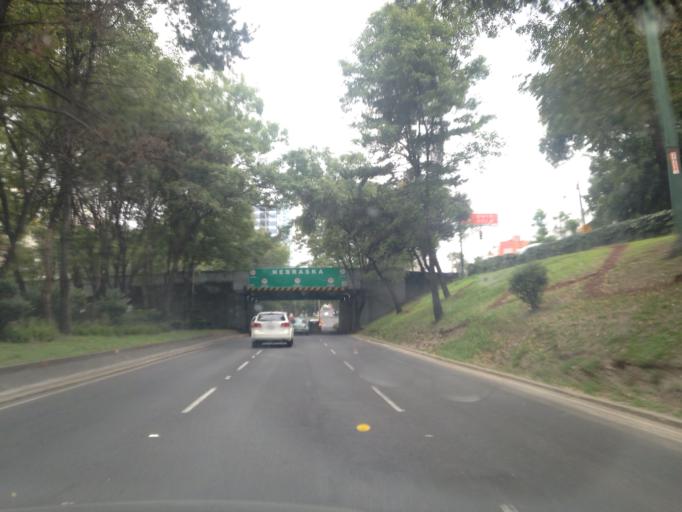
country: MX
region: Mexico City
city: Colonia del Valle
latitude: 19.3979
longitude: -99.1769
